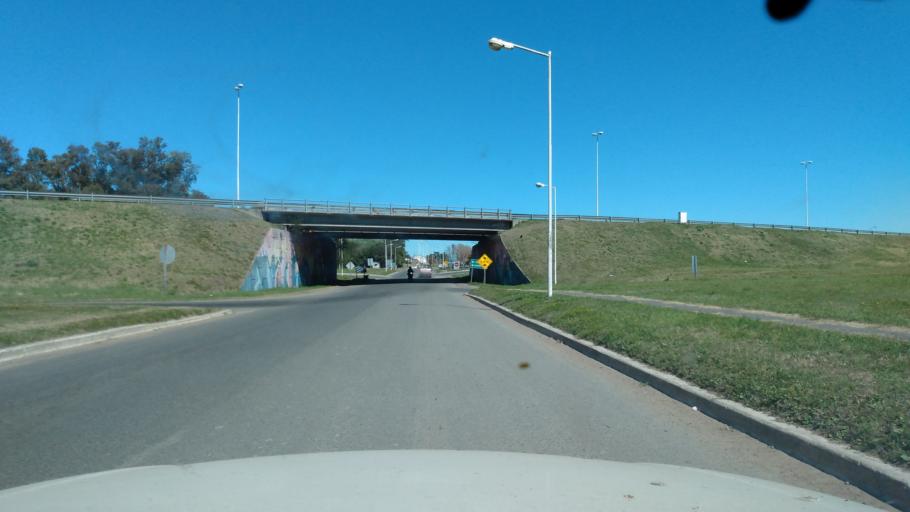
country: AR
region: Buenos Aires
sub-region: Partido de Lujan
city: Lujan
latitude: -34.5558
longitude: -59.0991
